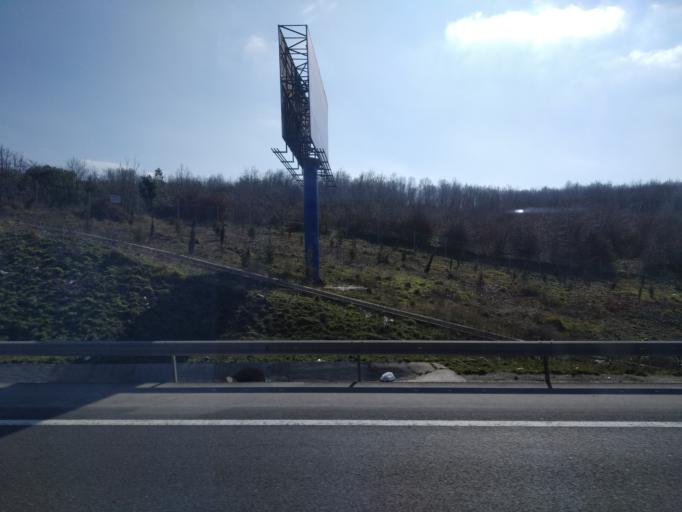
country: TR
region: Istanbul
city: Arikoey
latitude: 41.2305
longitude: 28.9403
